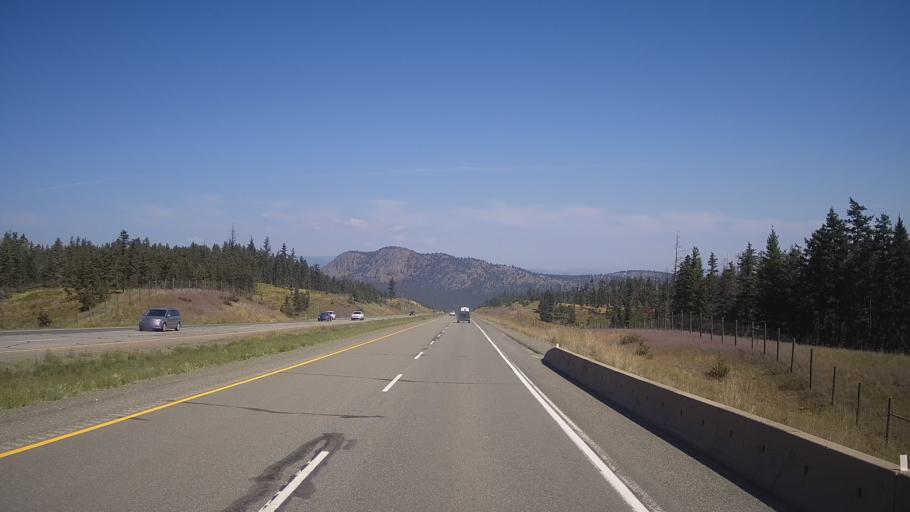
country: CA
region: British Columbia
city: Kamloops
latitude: 50.5964
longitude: -120.4770
